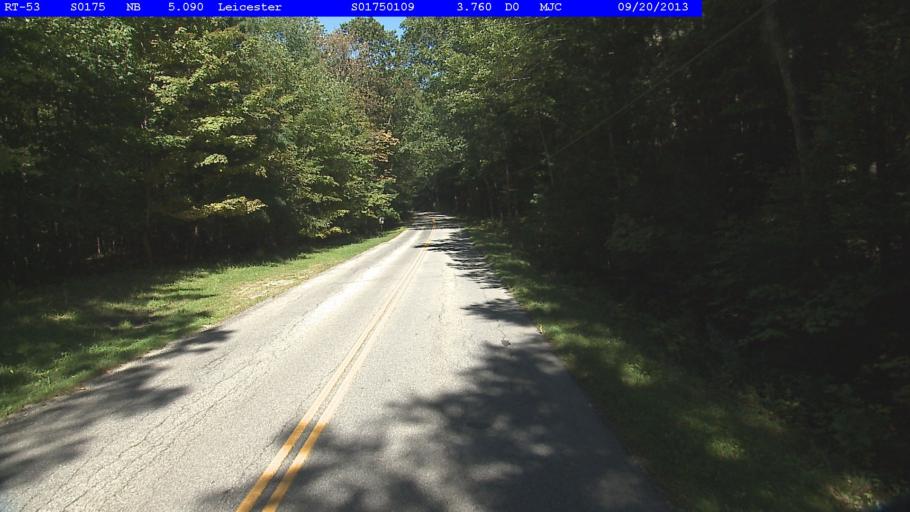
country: US
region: Vermont
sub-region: Rutland County
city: Brandon
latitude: 43.8967
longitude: -73.0640
